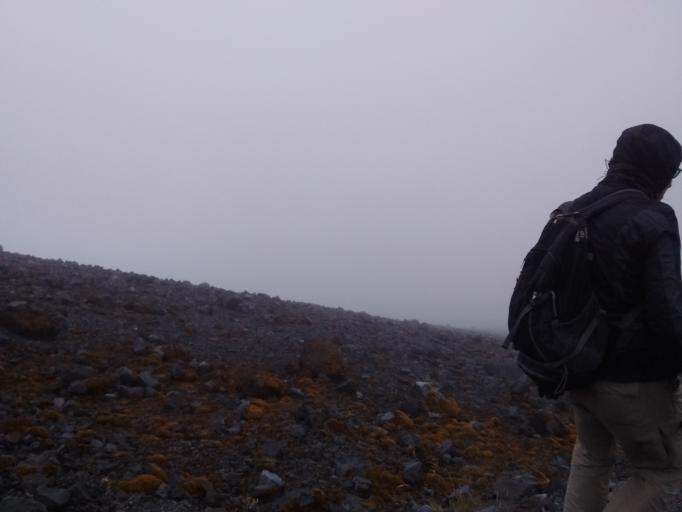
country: CO
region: Cauca
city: Totoro
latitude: 2.3191
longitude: -76.3942
